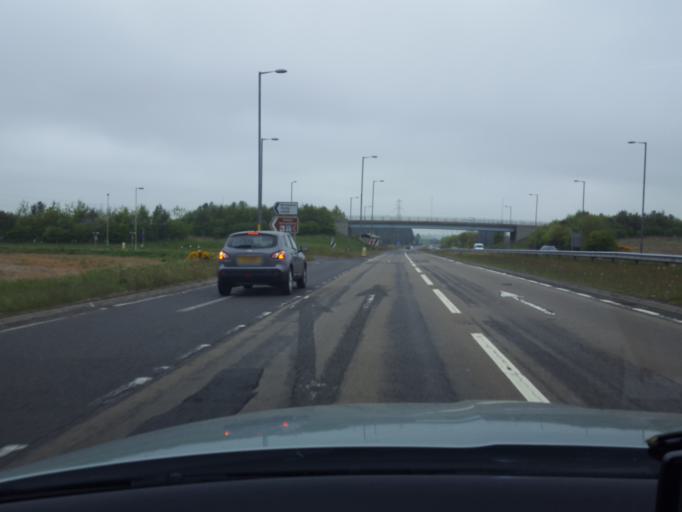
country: GB
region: Scotland
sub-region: Angus
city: Forfar
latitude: 56.6522
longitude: -2.9209
